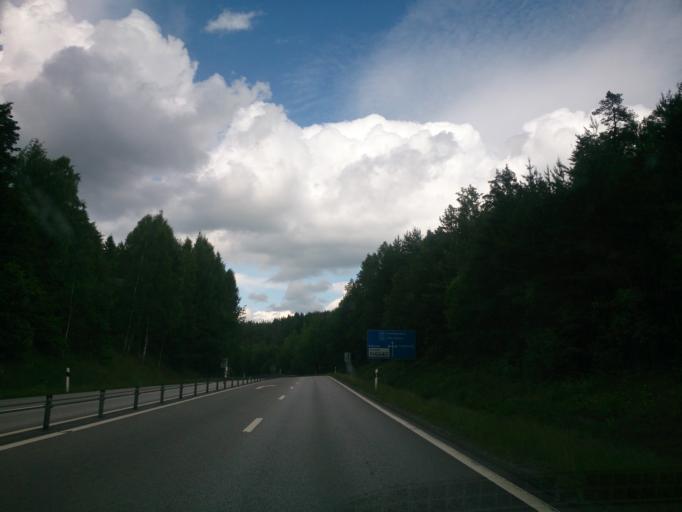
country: SE
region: OEstergoetland
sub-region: Norrkopings Kommun
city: Jursla
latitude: 58.6893
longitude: 16.1547
